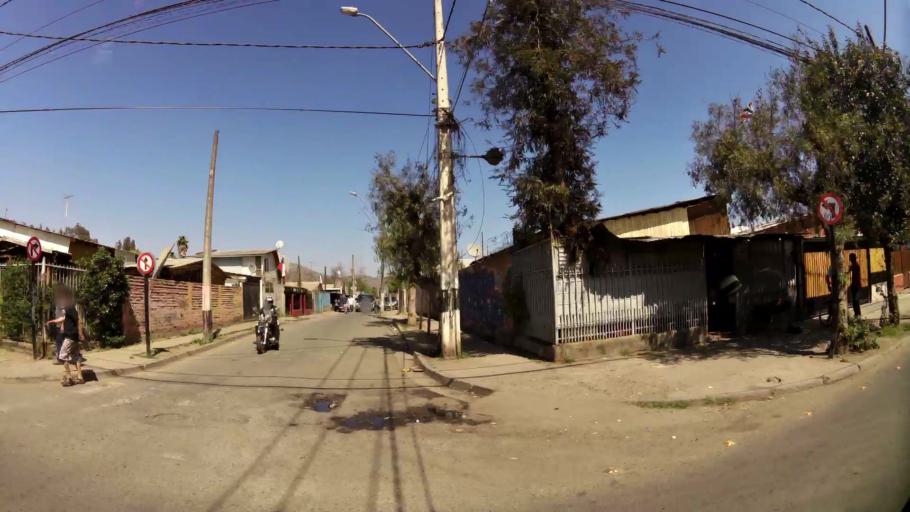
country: CL
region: Santiago Metropolitan
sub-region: Provincia de Santiago
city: Lo Prado
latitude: -33.3695
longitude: -70.7418
